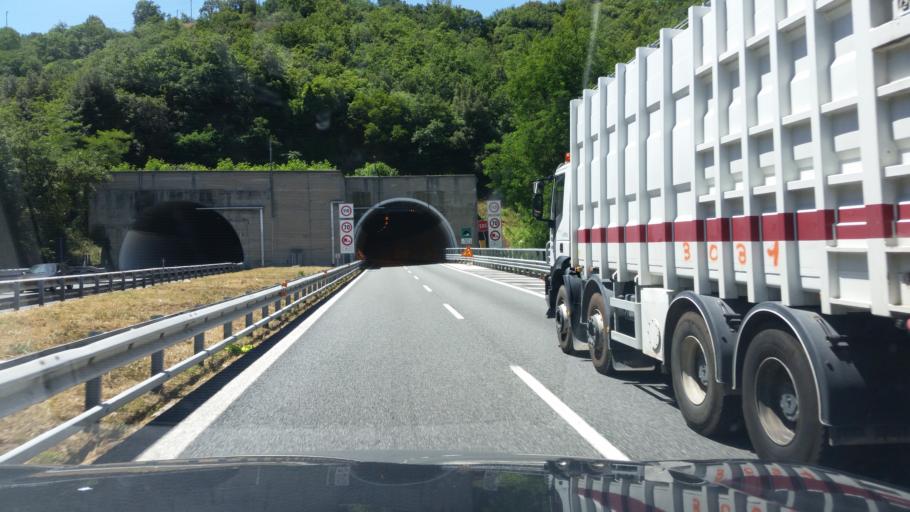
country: IT
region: Liguria
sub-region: Provincia di Savona
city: Savona
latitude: 44.3230
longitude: 8.4872
